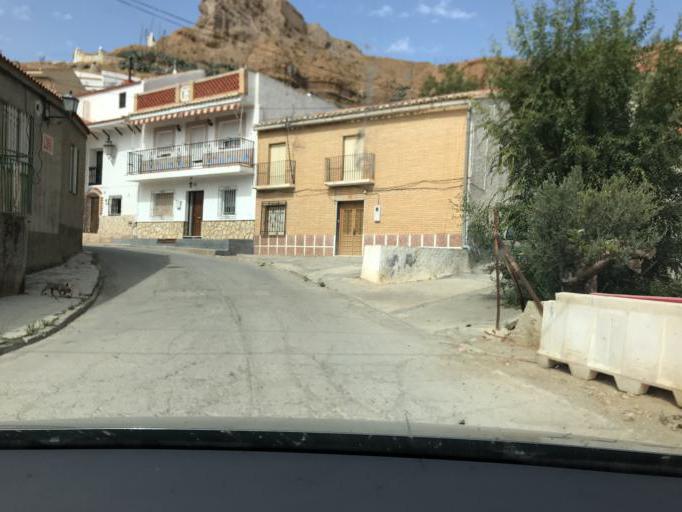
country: ES
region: Andalusia
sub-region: Provincia de Granada
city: Villanueva de las Torres
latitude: 37.4800
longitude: -3.0425
